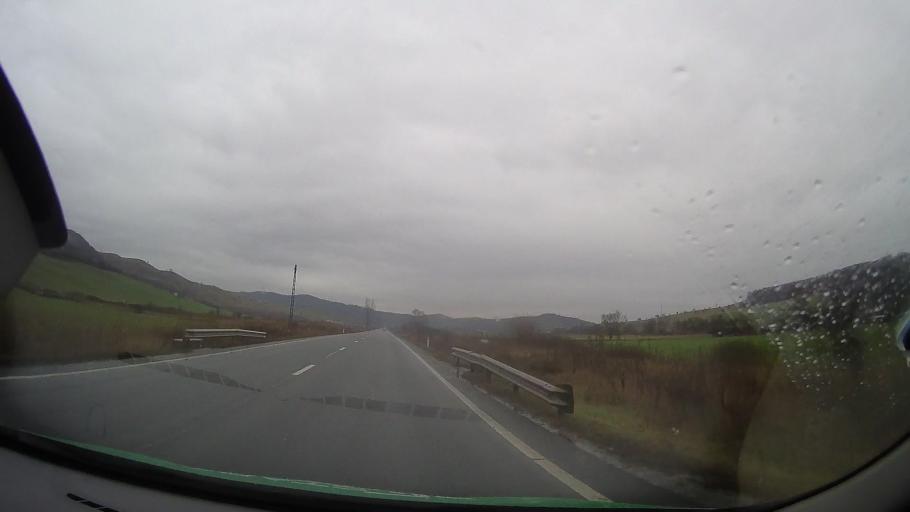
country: RO
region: Bistrita-Nasaud
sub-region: Comuna Teaca
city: Teaca
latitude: 46.9303
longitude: 24.4823
